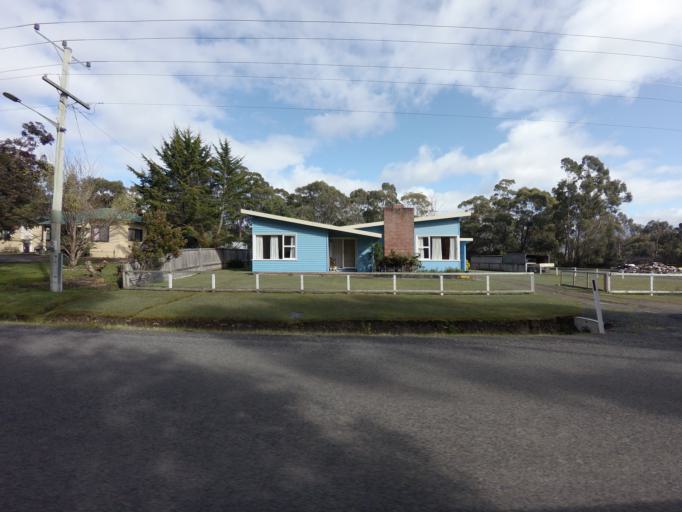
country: AU
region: Tasmania
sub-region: Huon Valley
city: Geeveston
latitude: -43.4400
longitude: 146.9039
